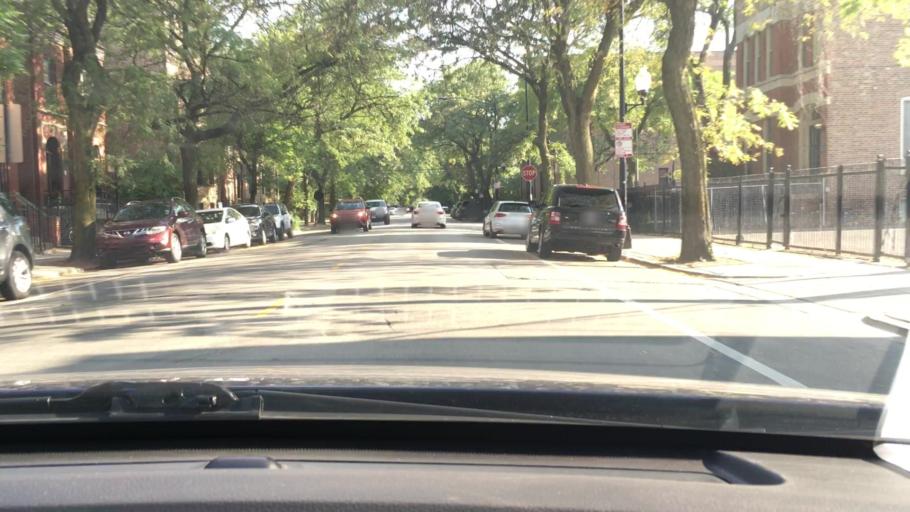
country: US
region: Illinois
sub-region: Cook County
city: Chicago
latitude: 41.8730
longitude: -87.6618
